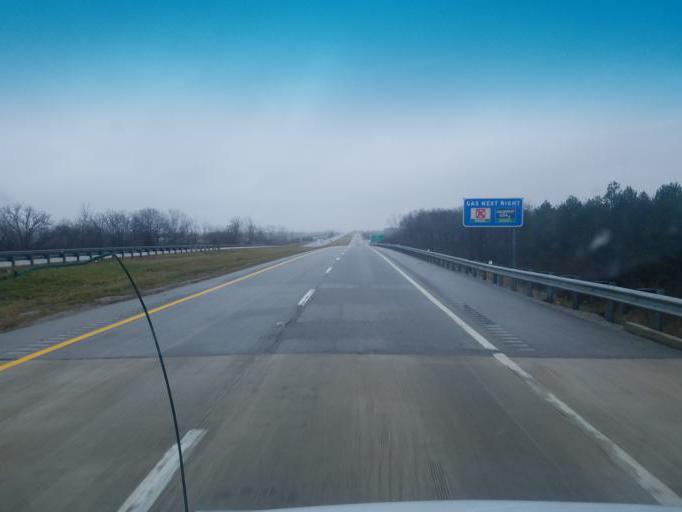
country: US
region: Ohio
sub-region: Wood County
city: Bowling Green
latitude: 41.3490
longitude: -83.6598
